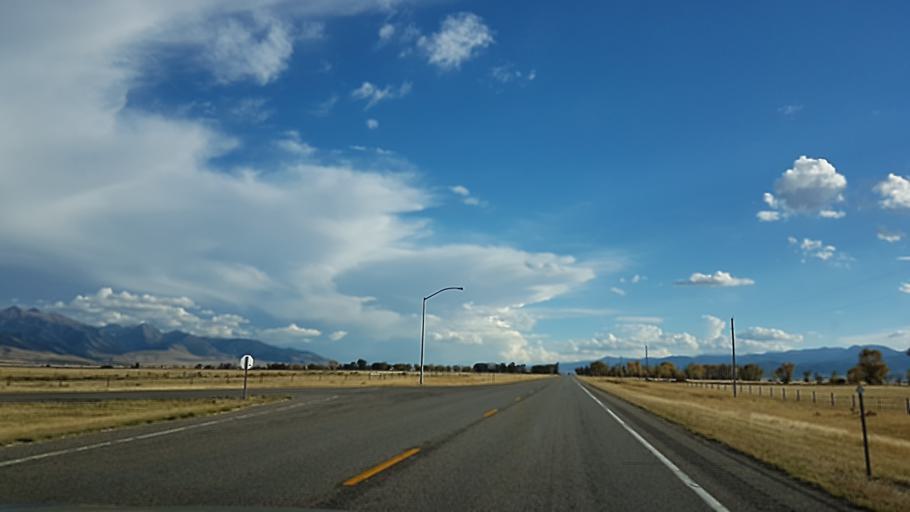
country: US
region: Montana
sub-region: Madison County
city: Virginia City
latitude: 45.2132
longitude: -111.6789
